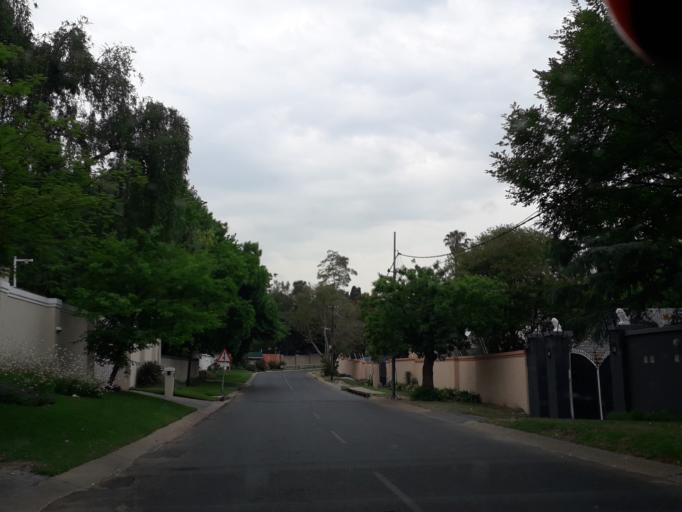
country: ZA
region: Gauteng
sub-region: City of Johannesburg Metropolitan Municipality
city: Modderfontein
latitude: -26.1162
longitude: 28.0797
